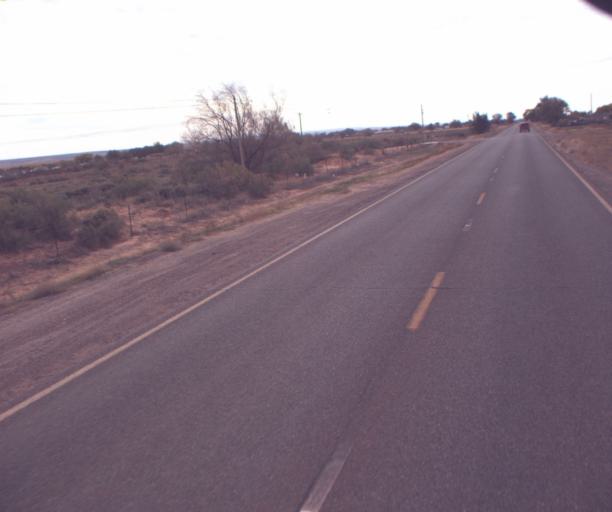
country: US
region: Arizona
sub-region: Apache County
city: Chinle
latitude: 36.2450
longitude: -109.6033
